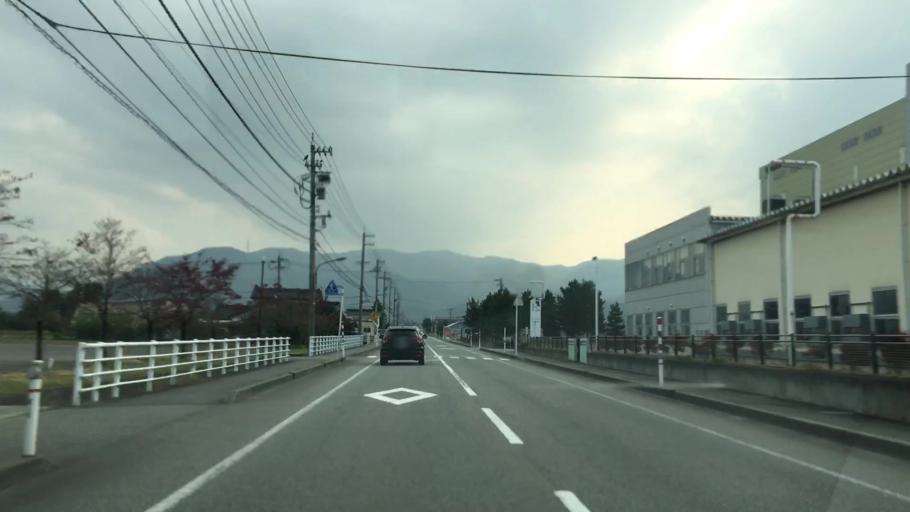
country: JP
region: Toyama
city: Yatsuomachi-higashikumisaka
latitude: 36.5883
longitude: 137.1908
